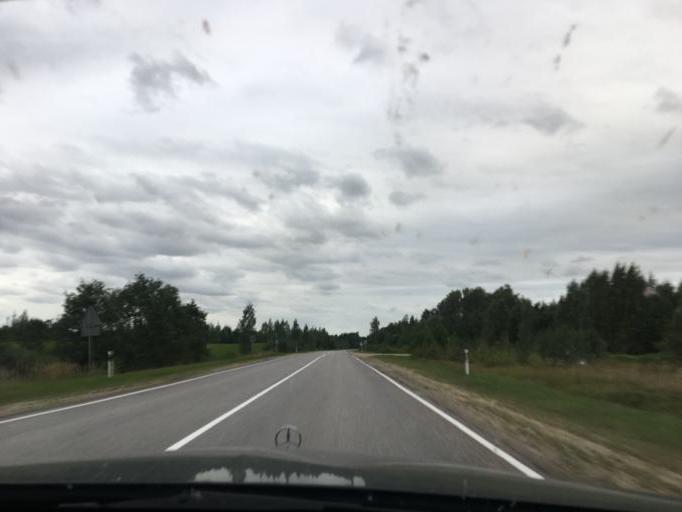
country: LV
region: Smiltene
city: Smiltene
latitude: 57.4299
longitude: 26.1429
